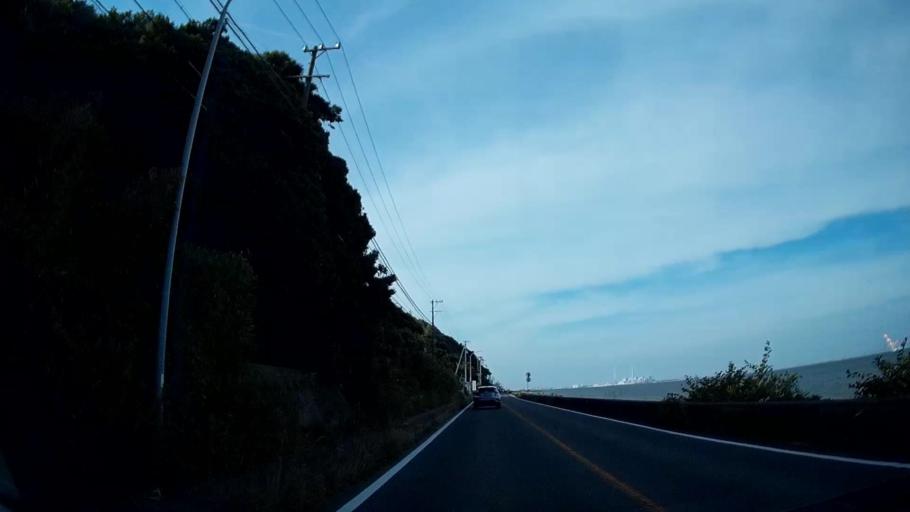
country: JP
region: Aichi
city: Taketoyo
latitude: 34.7863
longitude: 136.9171
